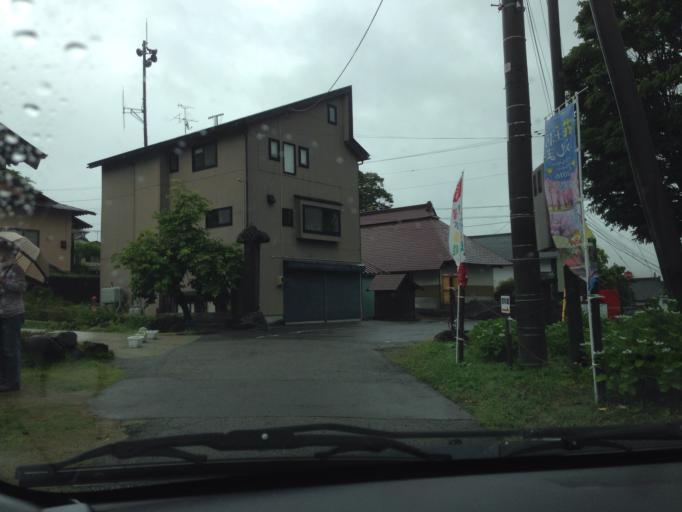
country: JP
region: Fukushima
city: Inawashiro
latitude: 37.5678
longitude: 139.9872
